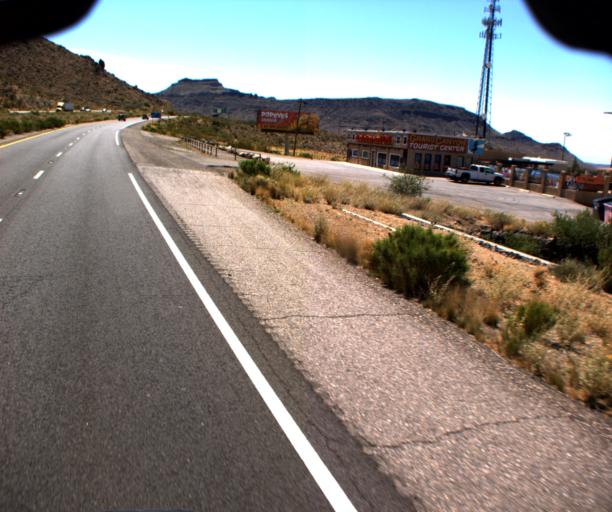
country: US
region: Arizona
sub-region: Mohave County
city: Golden Valley
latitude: 35.2348
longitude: -114.1397
